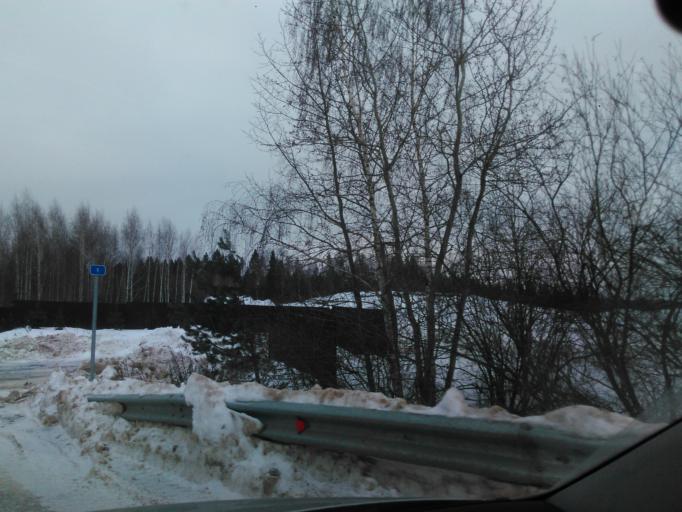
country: RU
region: Moskovskaya
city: Podosinki
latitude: 56.2740
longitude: 37.6107
